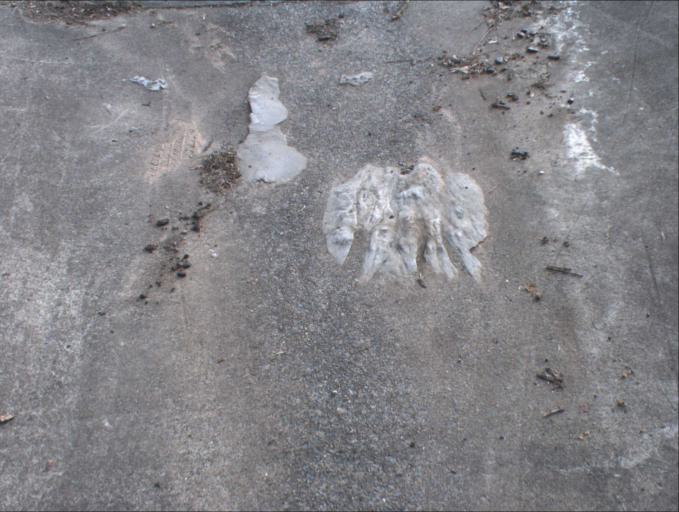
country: AU
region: Queensland
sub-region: Brisbane
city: Forest Lake
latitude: -27.6621
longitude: 152.9926
